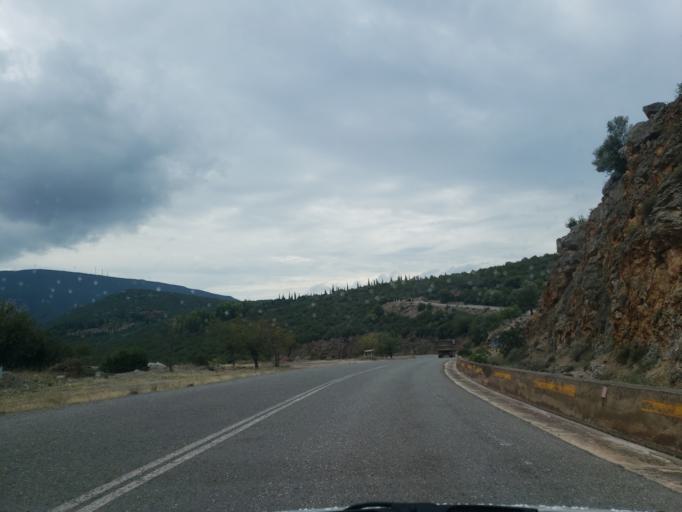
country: GR
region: Central Greece
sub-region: Nomos Fokidos
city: Amfissa
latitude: 38.5462
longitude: 22.4077
